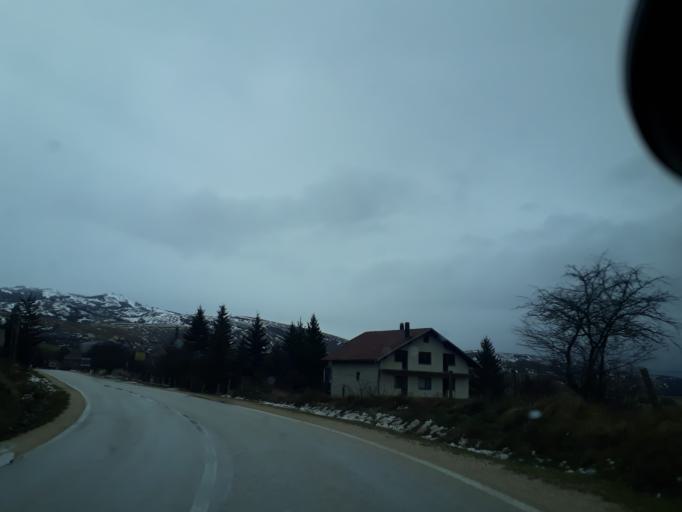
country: BA
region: Federation of Bosnia and Herzegovina
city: Tomislavgrad
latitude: 43.8384
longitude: 17.1795
